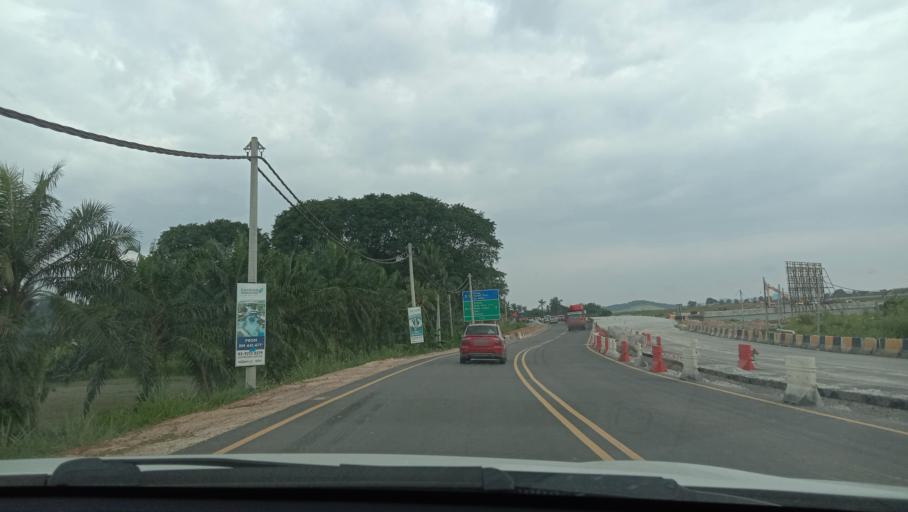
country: MY
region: Selangor
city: Batu Arang
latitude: 3.2651
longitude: 101.4574
